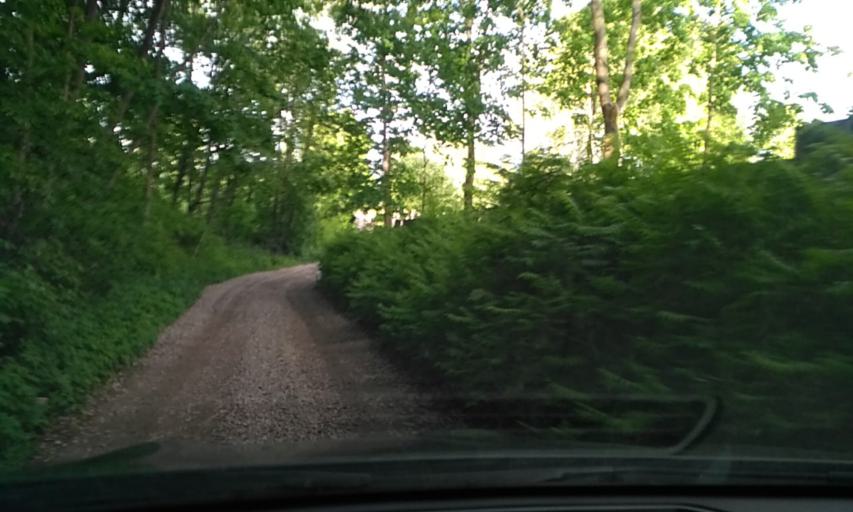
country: RU
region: Leningrad
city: Otradnoye
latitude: 59.8059
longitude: 30.8196
